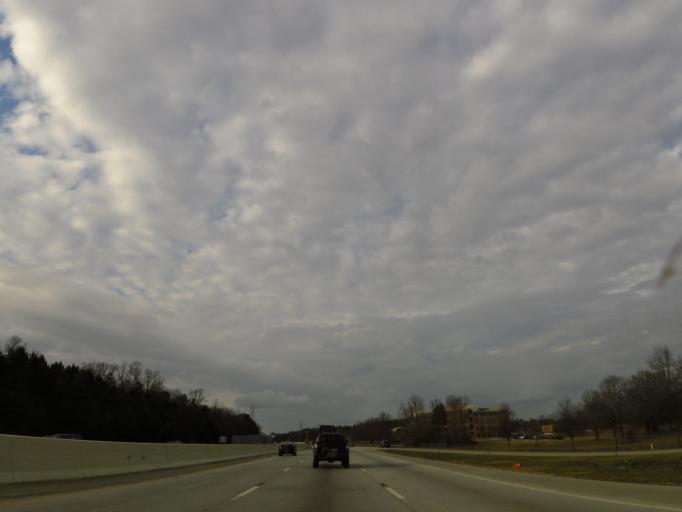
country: US
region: South Carolina
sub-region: Greenville County
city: Mauldin
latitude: 34.7921
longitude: -82.2803
